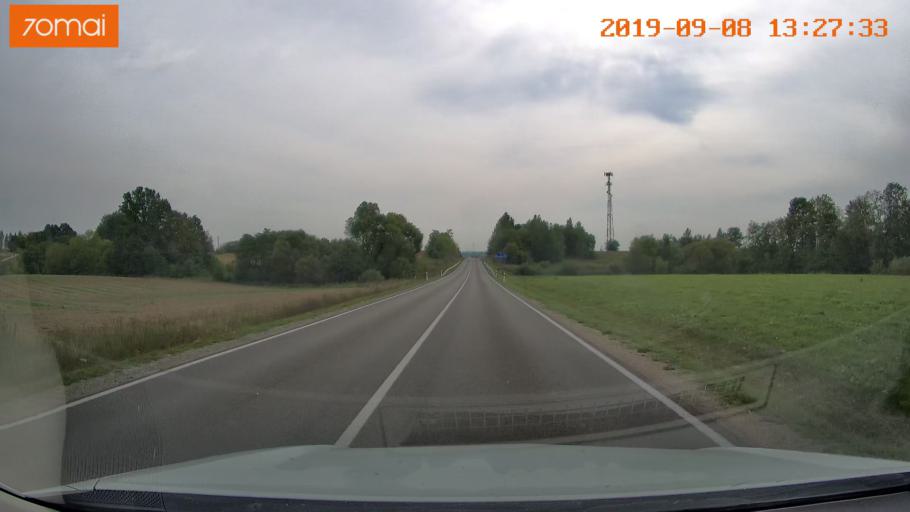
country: LT
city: Jieznas
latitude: 54.5850
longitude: 24.1681
